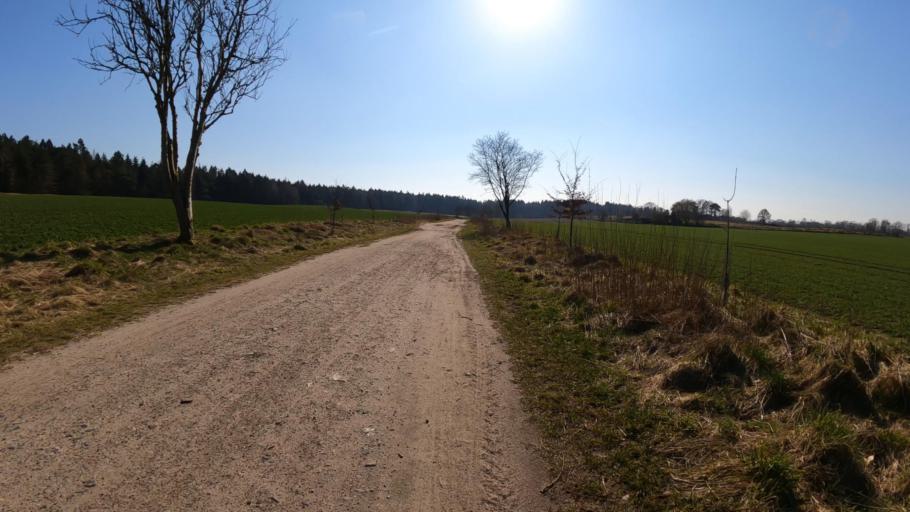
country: DE
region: Lower Saxony
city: Bendestorf
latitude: 53.3451
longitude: 9.9167
